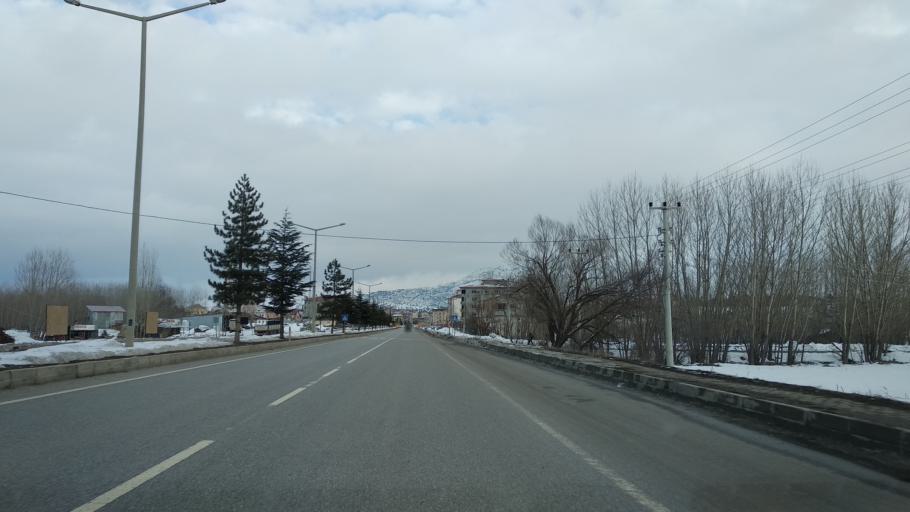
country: TR
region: Kahramanmaras
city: Goksun
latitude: 38.0266
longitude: 36.4896
